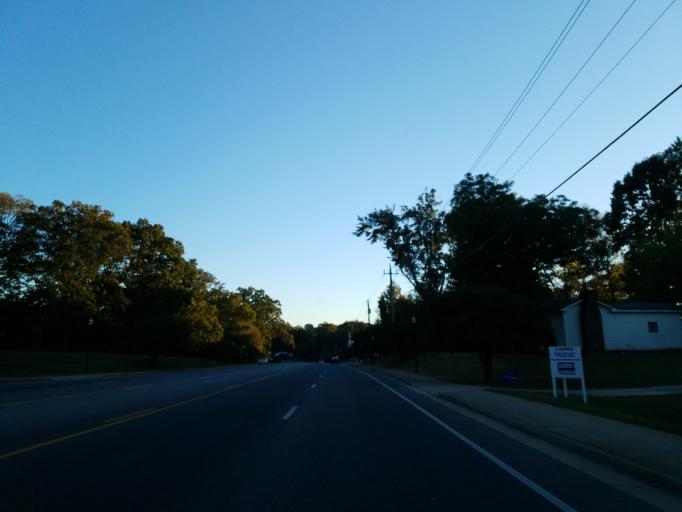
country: US
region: Georgia
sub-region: Forsyth County
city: Cumming
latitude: 34.2002
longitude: -84.1403
